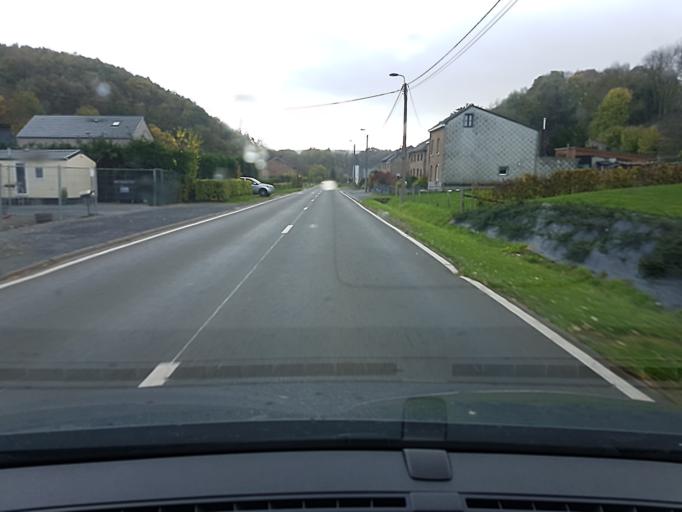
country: BE
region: Wallonia
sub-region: Province de Liege
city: Aywaille
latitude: 50.4944
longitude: 5.7203
